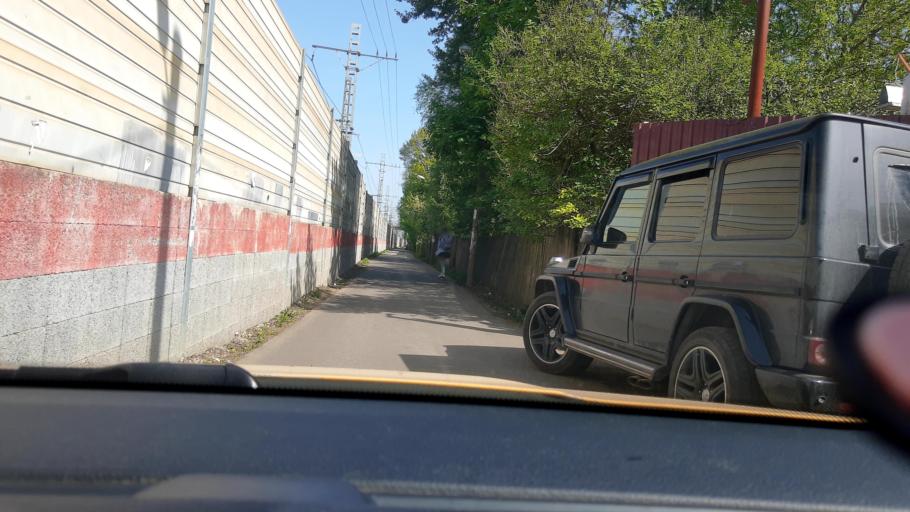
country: RU
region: Moskovskaya
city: Skhodnya
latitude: 55.9485
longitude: 37.3036
